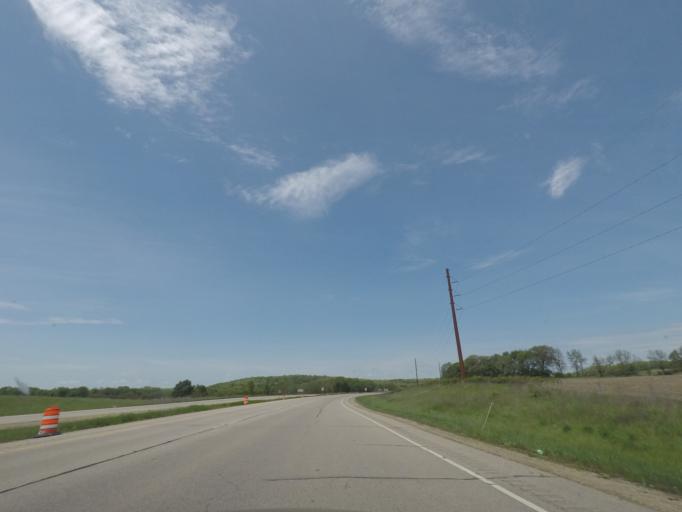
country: US
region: Wisconsin
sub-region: Dane County
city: Oregon
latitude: 42.9549
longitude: -89.3829
